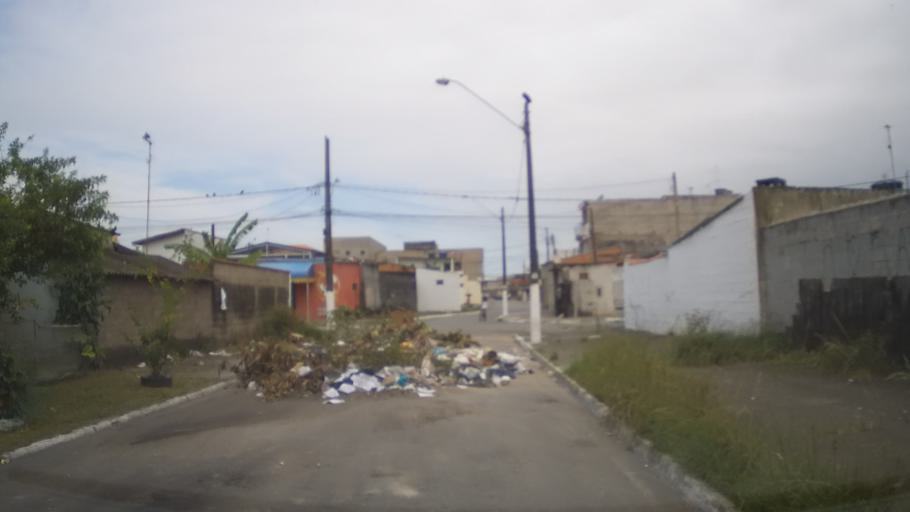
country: BR
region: Sao Paulo
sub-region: Praia Grande
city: Praia Grande
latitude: -24.0173
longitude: -46.4906
